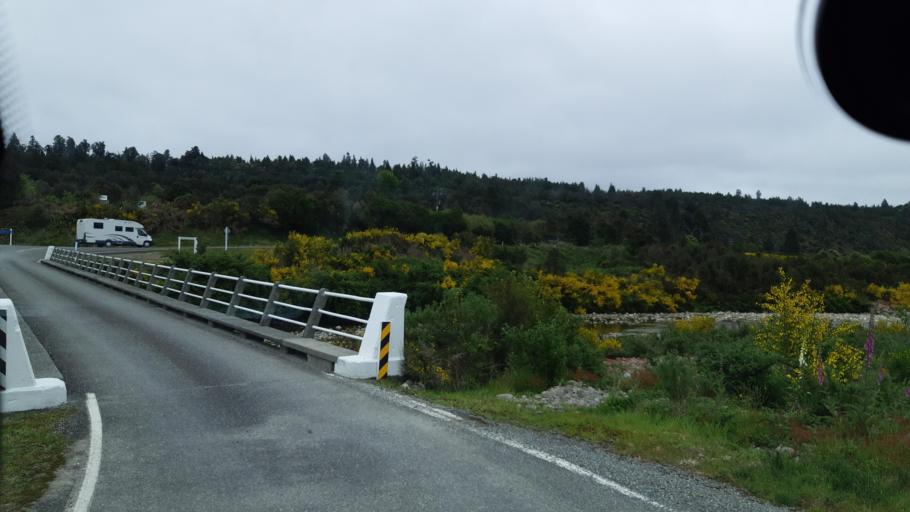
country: NZ
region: West Coast
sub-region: Grey District
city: Greymouth
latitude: -42.6345
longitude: 171.2788
